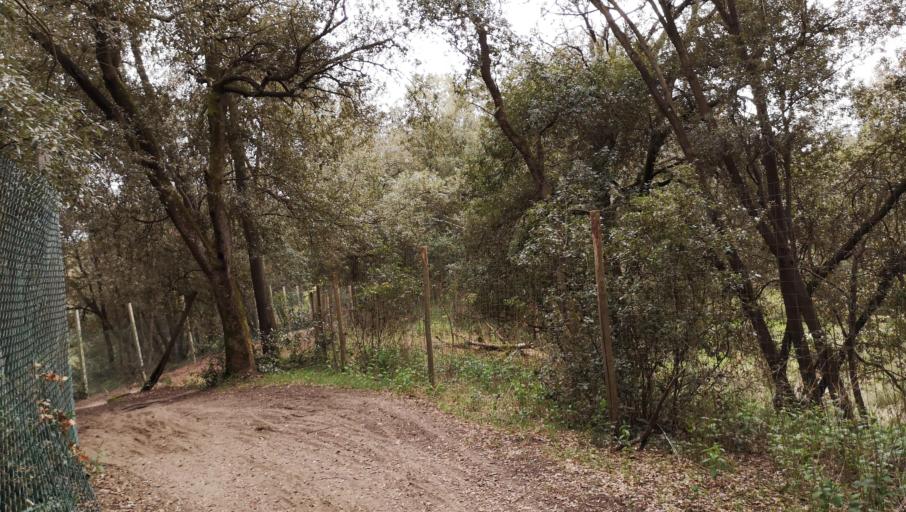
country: IT
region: Emilia-Romagna
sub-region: Provincia di Ferrara
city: Goro
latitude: 44.8187
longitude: 12.2610
